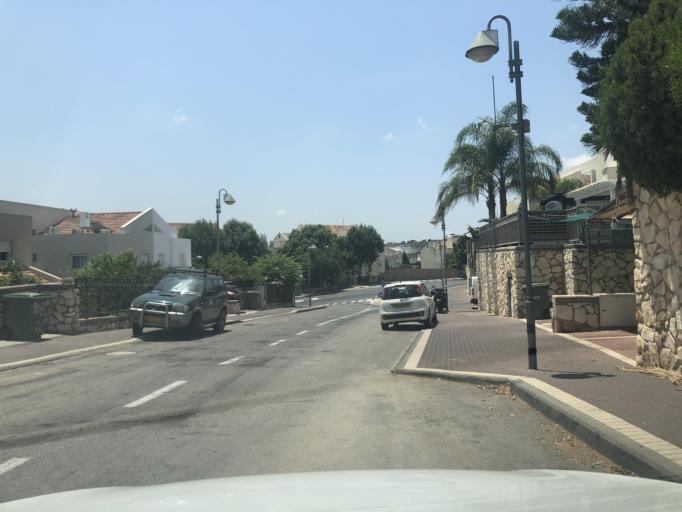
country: IL
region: Haifa
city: Daliyat el Karmil
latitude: 32.6386
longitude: 35.0922
